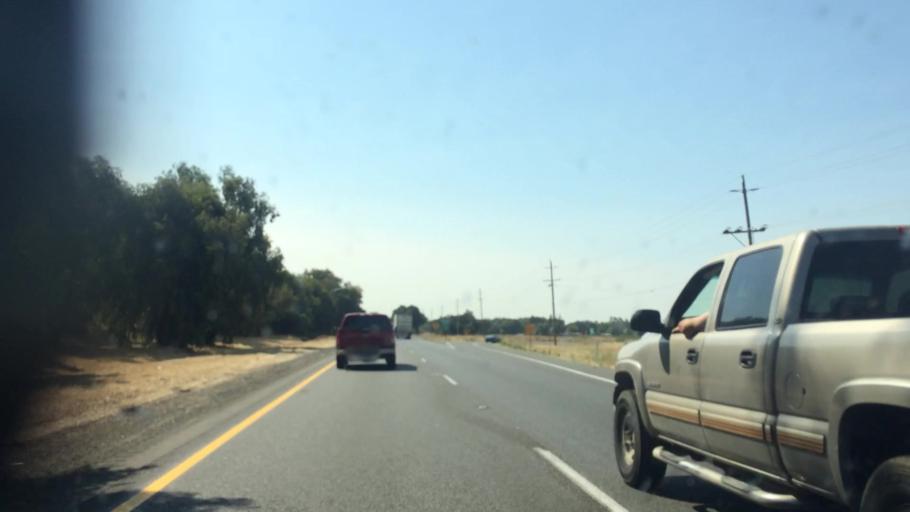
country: US
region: California
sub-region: Sacramento County
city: Elk Grove
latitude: 38.3650
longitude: -121.3507
